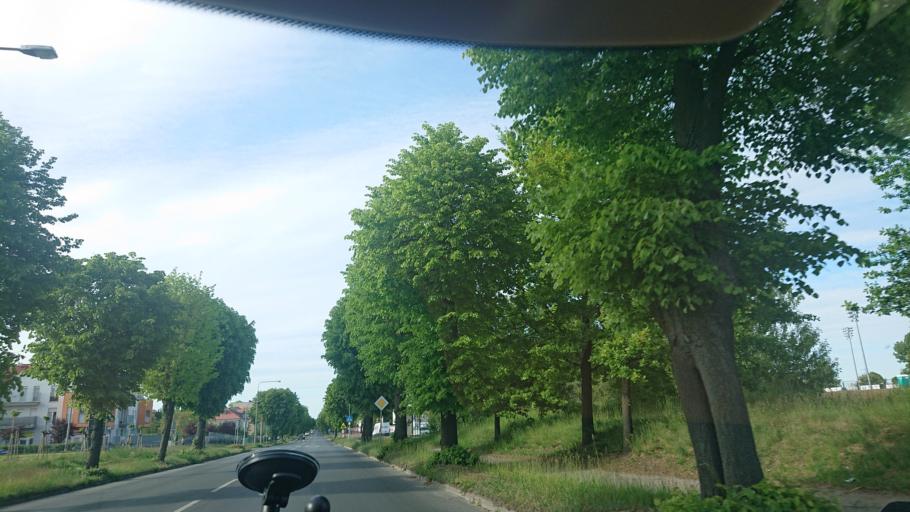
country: PL
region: Greater Poland Voivodeship
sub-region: Powiat gnieznienski
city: Gniezno
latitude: 52.5200
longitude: 17.5962
